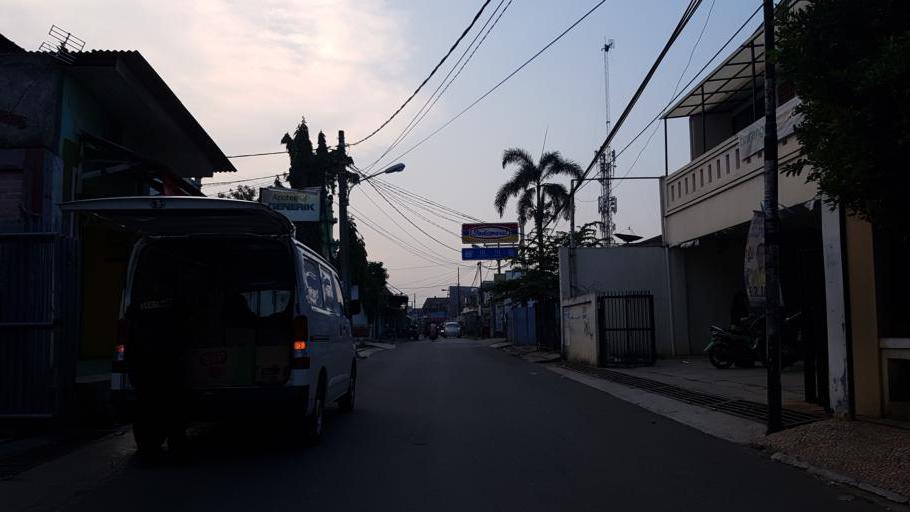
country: ID
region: West Java
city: Bekasi
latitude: -6.2657
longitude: 106.9461
